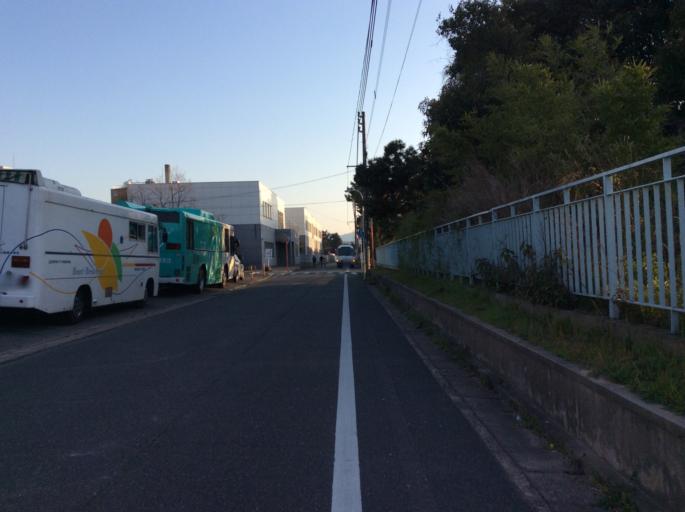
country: JP
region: Fukuoka
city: Fukuoka-shi
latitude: 33.6275
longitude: 130.4241
